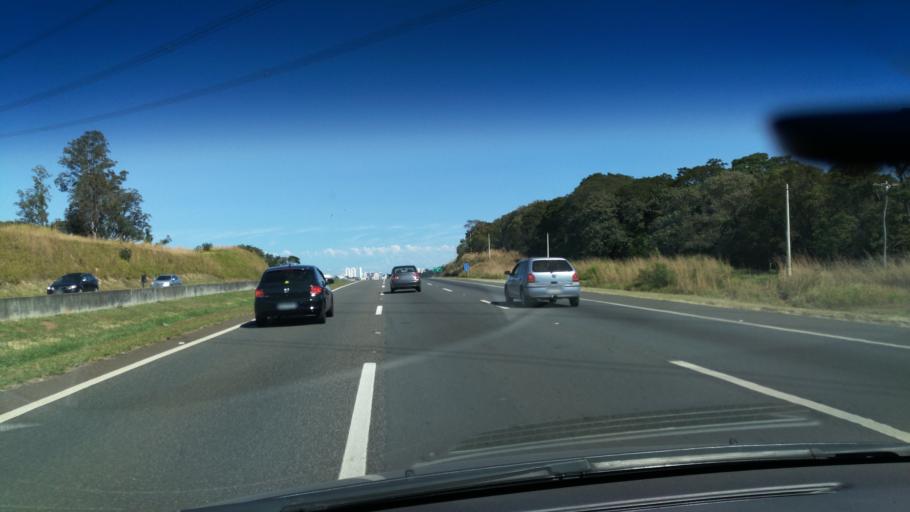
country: BR
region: Sao Paulo
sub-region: Campinas
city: Campinas
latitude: -22.8085
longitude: -47.0338
